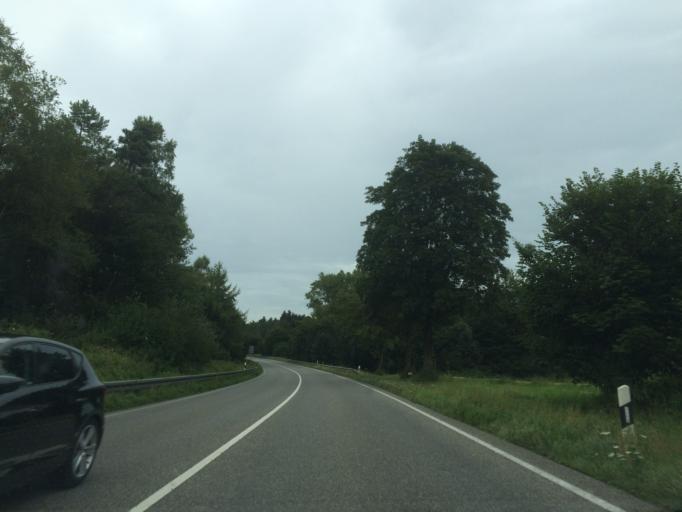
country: DE
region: Baden-Wuerttemberg
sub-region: Tuebingen Region
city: Bad Waldsee
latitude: 47.9168
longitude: 9.7701
